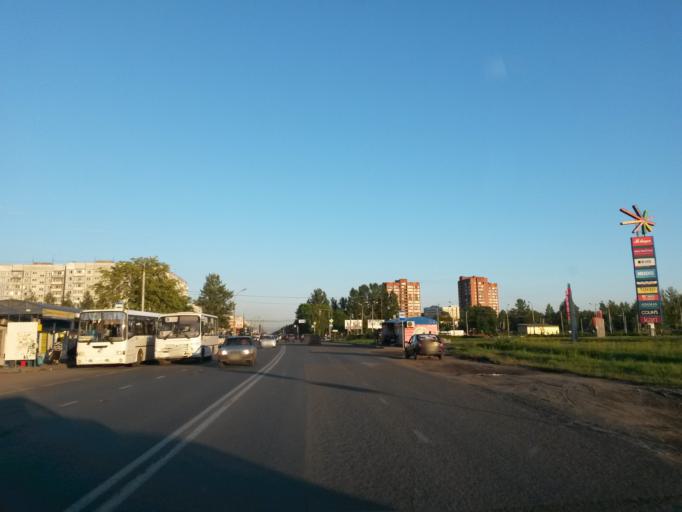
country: RU
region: Jaroslavl
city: Yaroslavl
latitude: 57.6989
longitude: 39.7625
